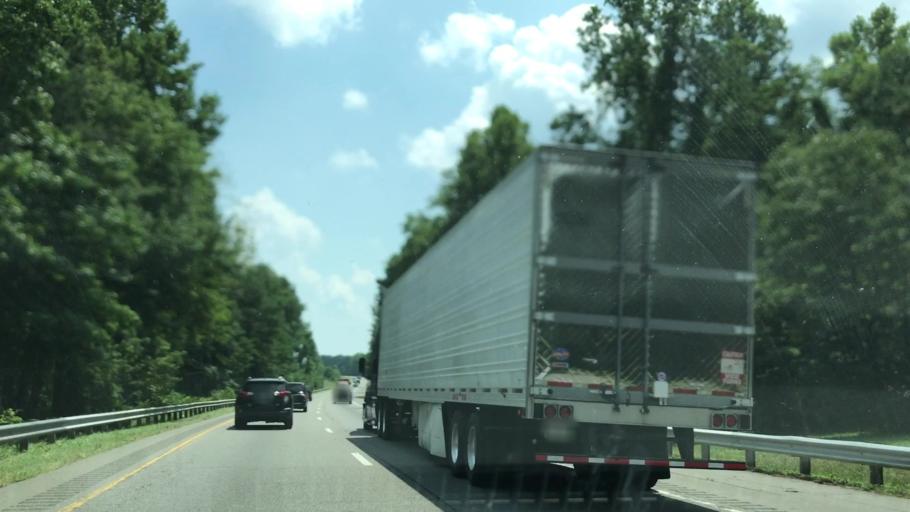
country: US
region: North Carolina
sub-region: Iredell County
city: Troutman
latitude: 35.7100
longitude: -80.8560
